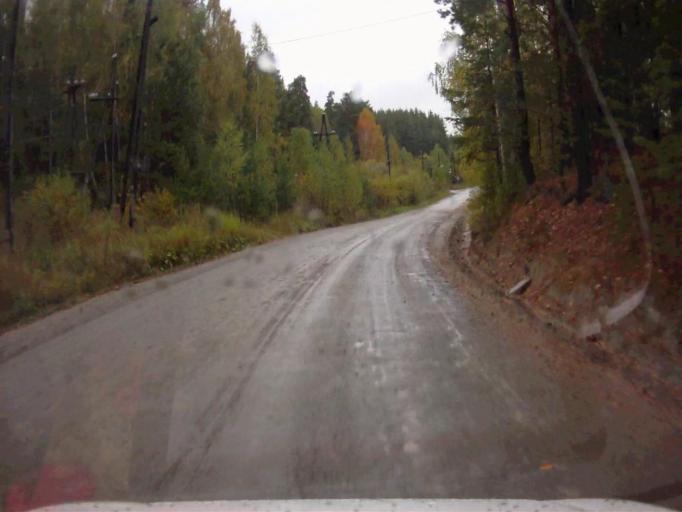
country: RU
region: Chelyabinsk
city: Kyshtym
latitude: 55.7439
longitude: 60.4928
